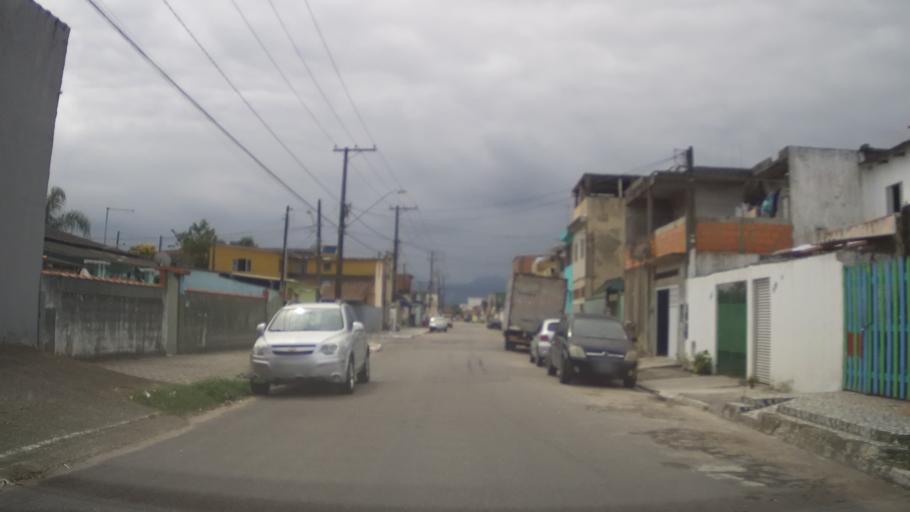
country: BR
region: Sao Paulo
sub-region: Praia Grande
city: Praia Grande
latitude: -24.0093
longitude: -46.4414
